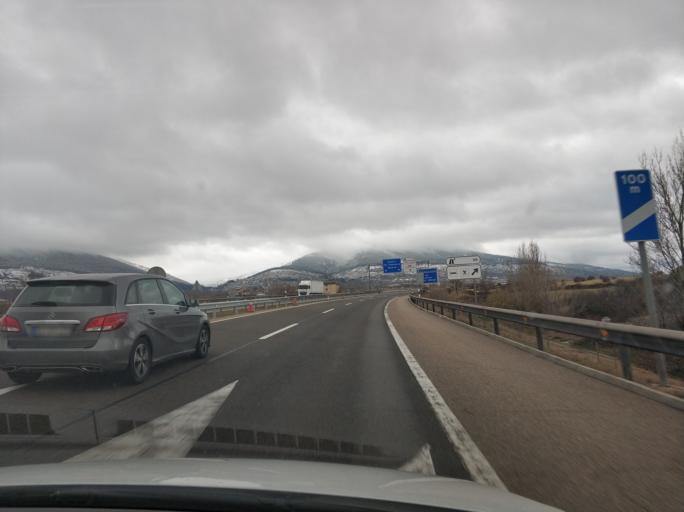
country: ES
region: Castille and Leon
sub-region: Provincia de Segovia
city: Cerezo de Abajo
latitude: 41.1974
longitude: -3.5824
